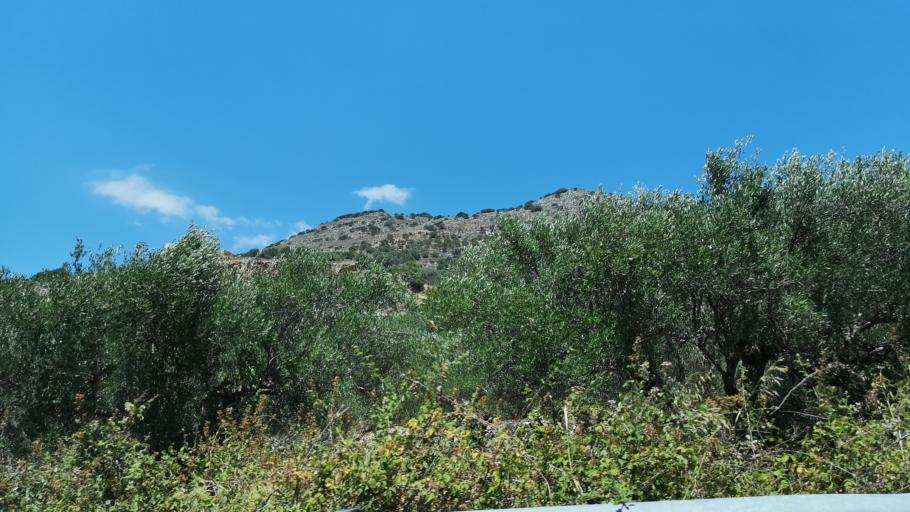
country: GR
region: Crete
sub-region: Nomos Lasithiou
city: Neapoli
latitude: 35.2490
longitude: 25.6236
